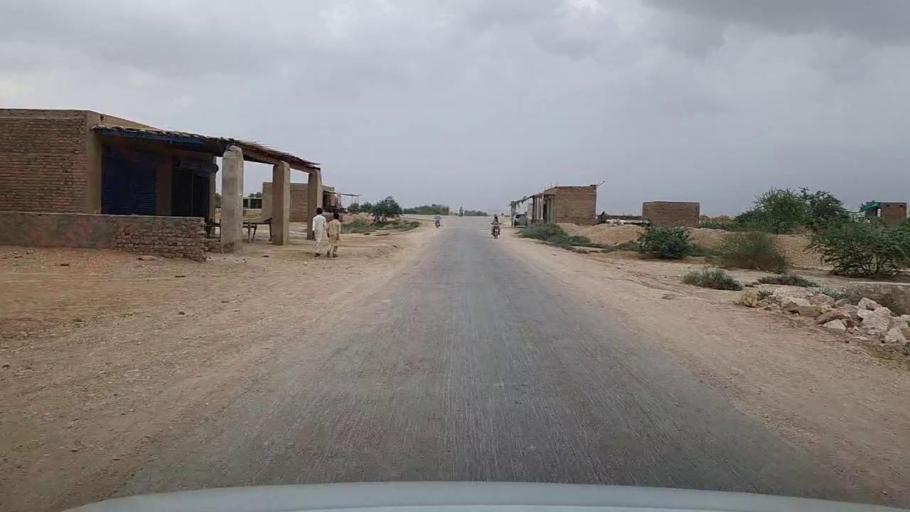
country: PK
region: Sindh
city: Sehwan
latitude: 26.3351
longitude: 67.7235
